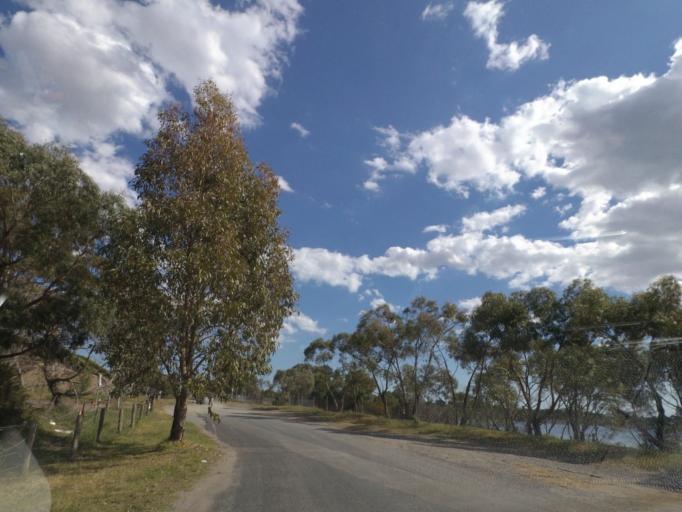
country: AU
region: Victoria
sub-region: Monash
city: Oakleigh South
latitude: -37.9407
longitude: 145.0885
